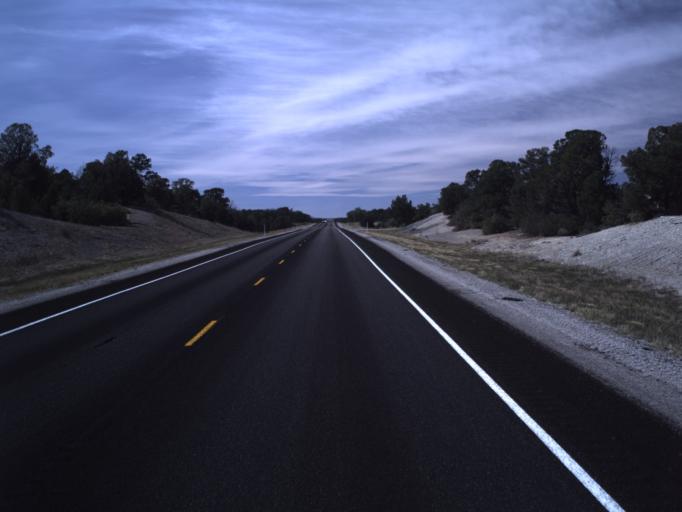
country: US
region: Colorado
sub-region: Dolores County
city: Dove Creek
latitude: 37.8285
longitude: -109.0838
